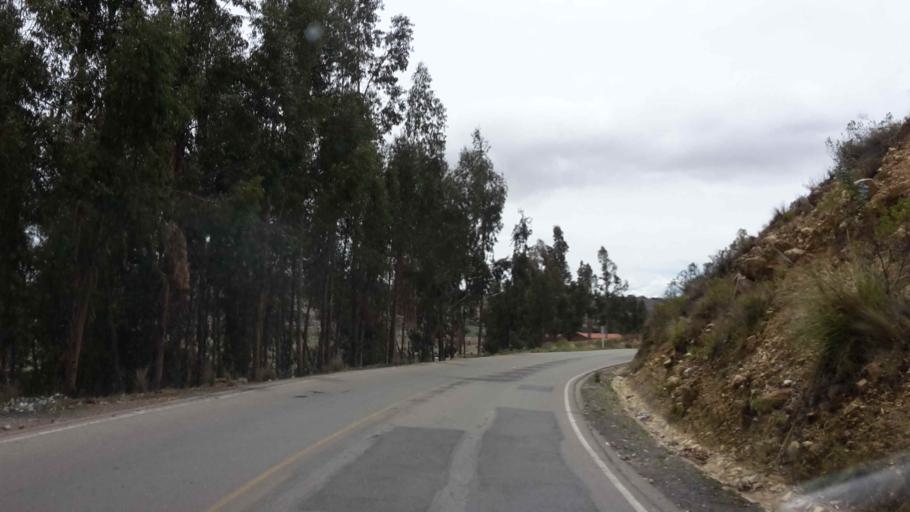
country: BO
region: Cochabamba
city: Arani
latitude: -17.4784
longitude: -65.6251
